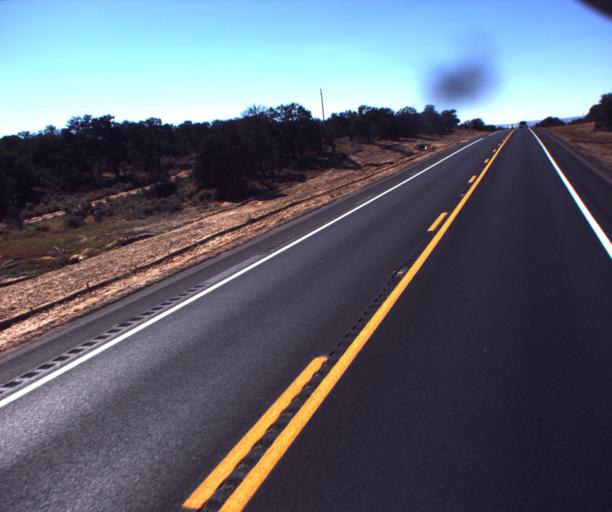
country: US
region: Arizona
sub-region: Apache County
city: Ganado
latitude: 35.7187
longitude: -109.3856
